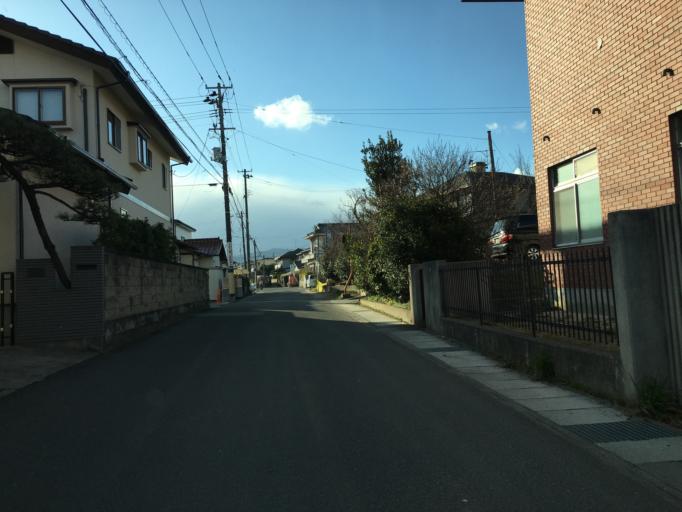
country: JP
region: Fukushima
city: Fukushima-shi
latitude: 37.7798
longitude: 140.4387
